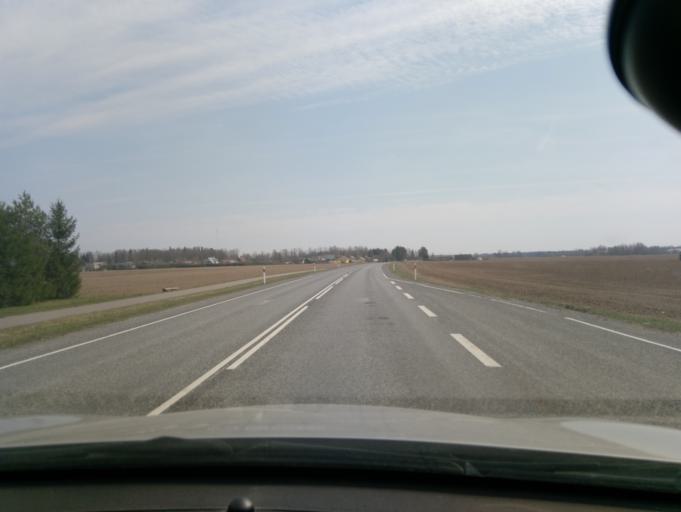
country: EE
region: Jaervamaa
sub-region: Paide linn
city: Paide
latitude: 58.7610
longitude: 25.5510
